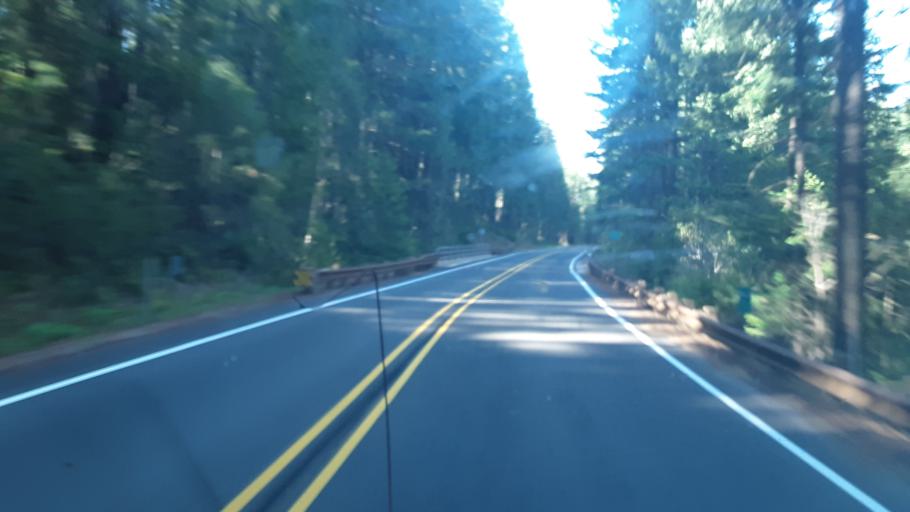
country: US
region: Oregon
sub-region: Jackson County
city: Shady Cove
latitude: 42.9340
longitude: -122.4217
